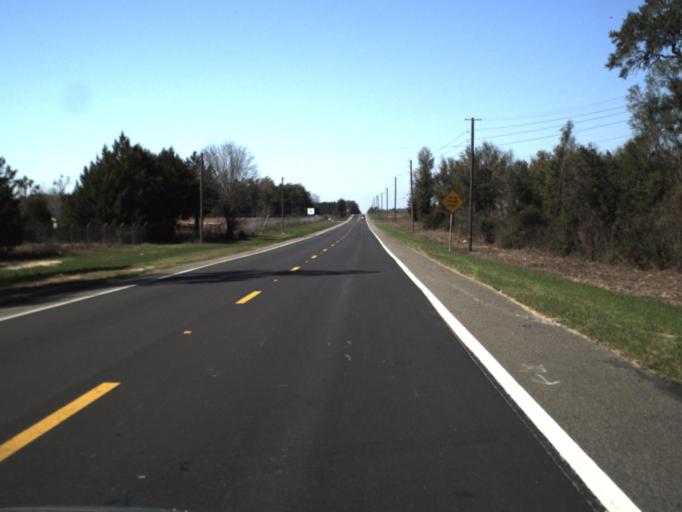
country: US
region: Florida
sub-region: Jackson County
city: Marianna
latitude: 30.6582
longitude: -85.1628
